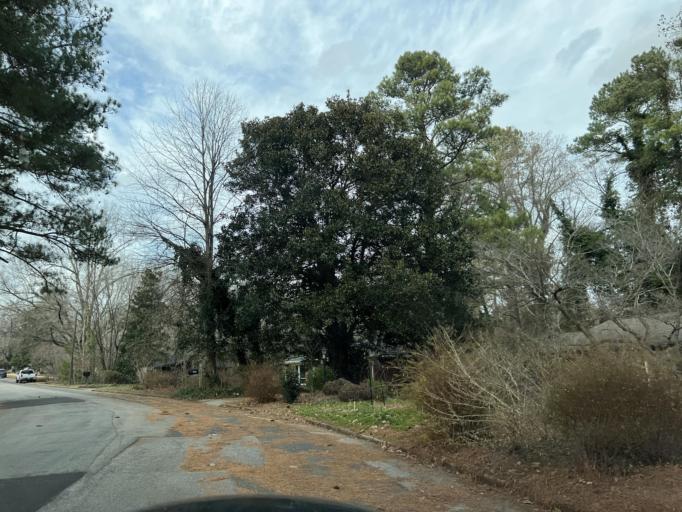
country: US
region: North Carolina
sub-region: Wake County
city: West Raleigh
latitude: 35.7725
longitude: -78.7065
